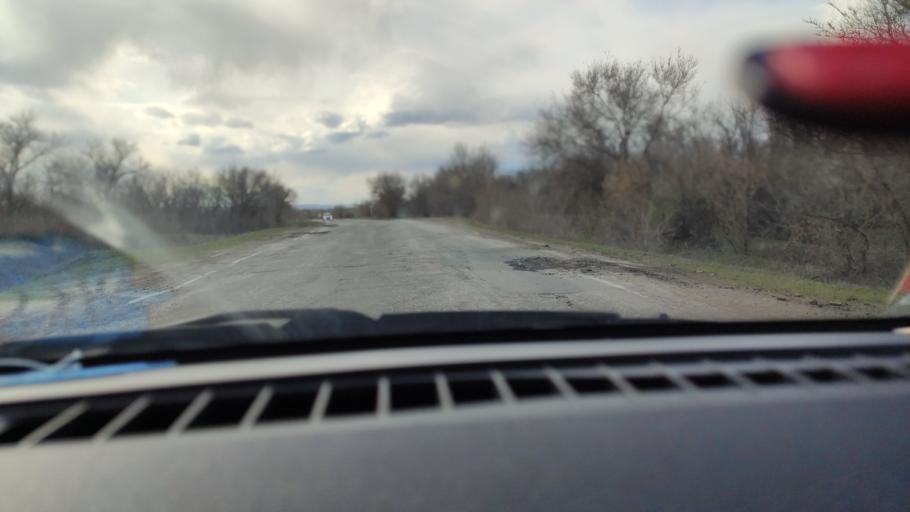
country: RU
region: Saratov
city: Rovnoye
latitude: 51.0457
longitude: 46.0540
